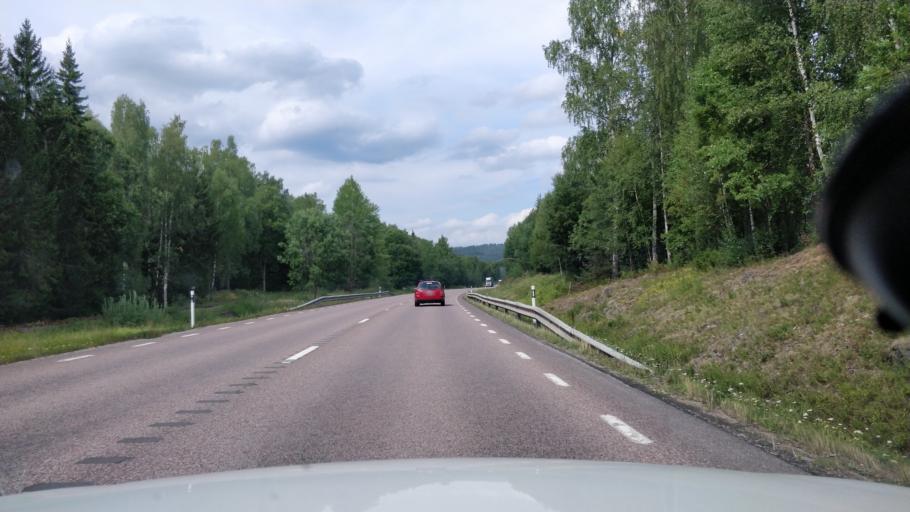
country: SE
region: Dalarna
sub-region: Faluns Kommun
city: Falun
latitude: 60.6530
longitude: 15.5577
